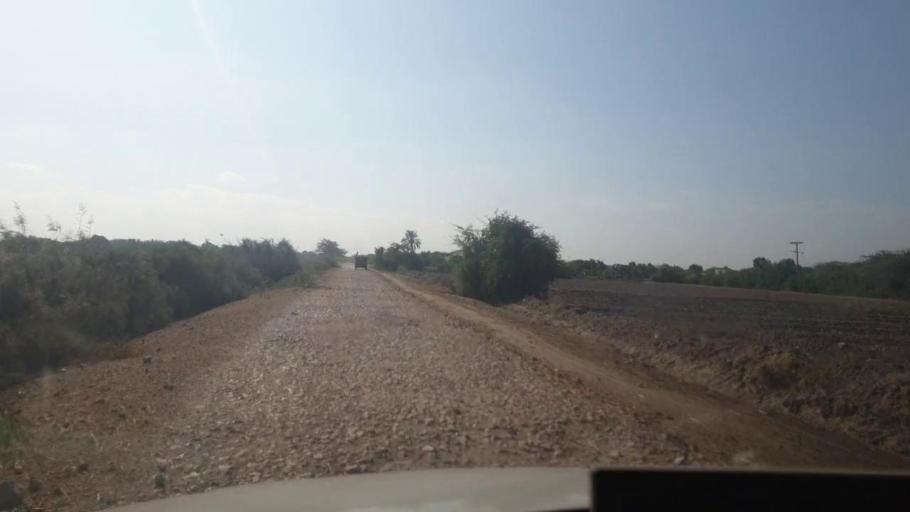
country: PK
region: Sindh
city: Mirpur Sakro
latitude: 24.4722
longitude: 67.5956
